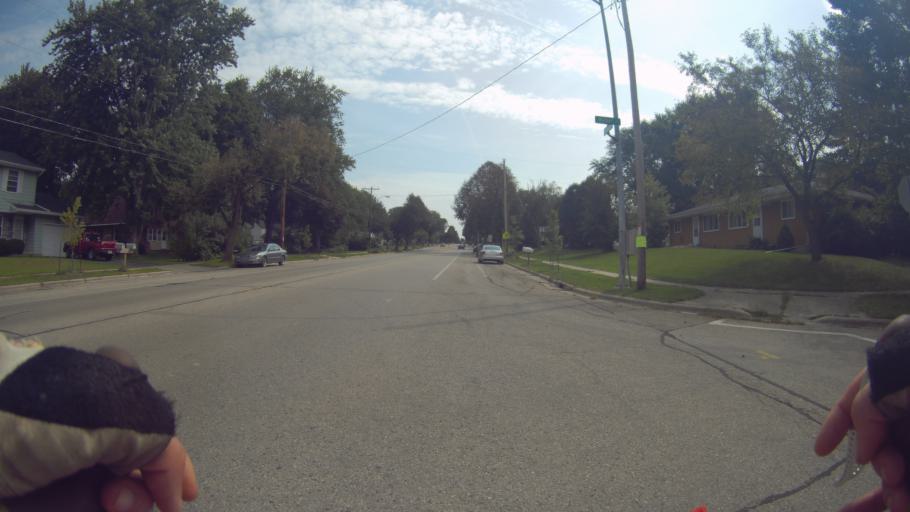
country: US
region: Wisconsin
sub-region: Dane County
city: Monona
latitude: 43.0988
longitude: -89.3002
